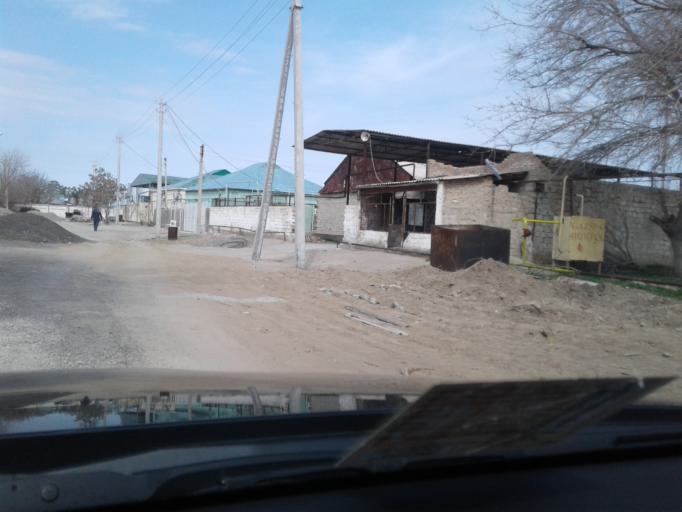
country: TM
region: Ahal
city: Abadan
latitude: 38.1214
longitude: 58.3485
